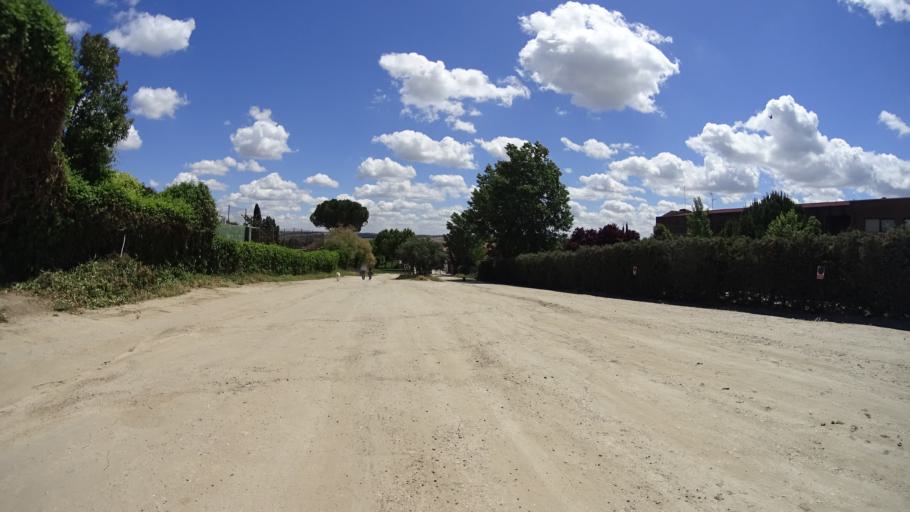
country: ES
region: Madrid
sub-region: Provincia de Madrid
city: Villanueva del Pardillo
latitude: 40.4665
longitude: -3.9578
